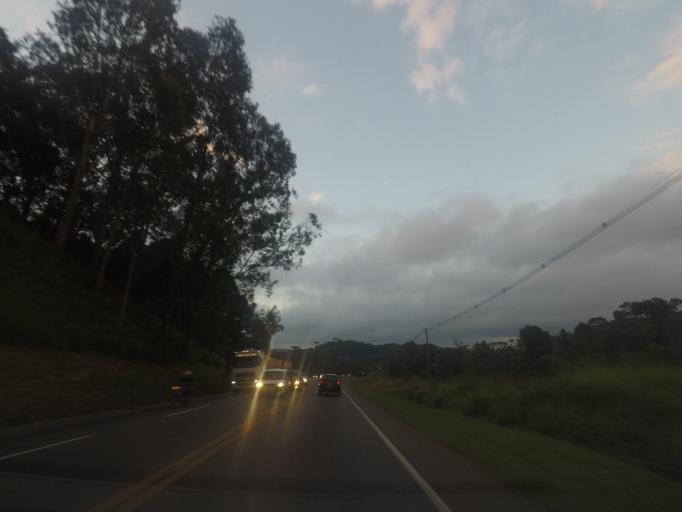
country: BR
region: Parana
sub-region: Almirante Tamandare
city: Almirante Tamandare
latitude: -25.3983
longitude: -49.3610
